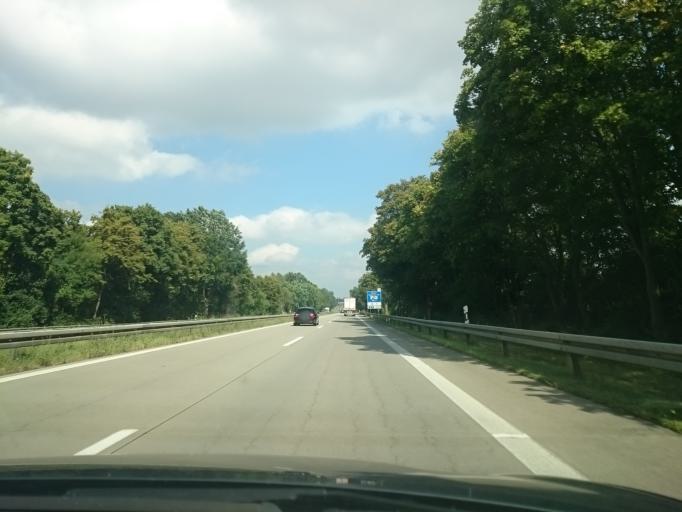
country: DE
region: Brandenburg
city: Marienwerder
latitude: 52.8725
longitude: 13.6901
